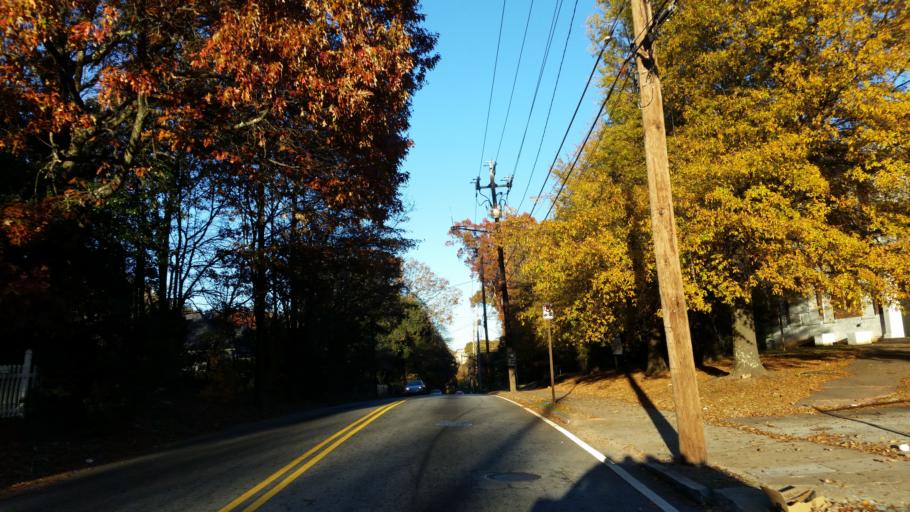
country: US
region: Georgia
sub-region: Fulton County
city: Atlanta
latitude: 33.7057
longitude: -84.3778
